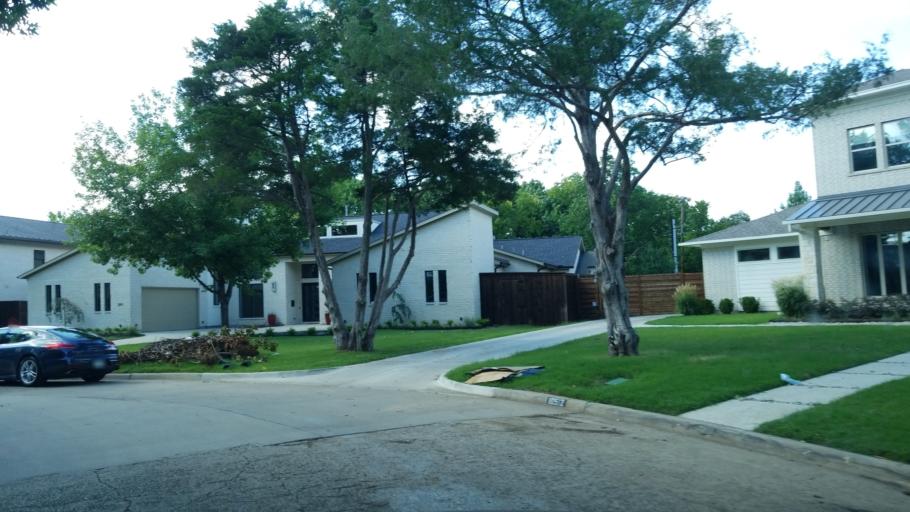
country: US
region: Texas
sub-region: Dallas County
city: University Park
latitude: 32.8892
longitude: -96.8418
